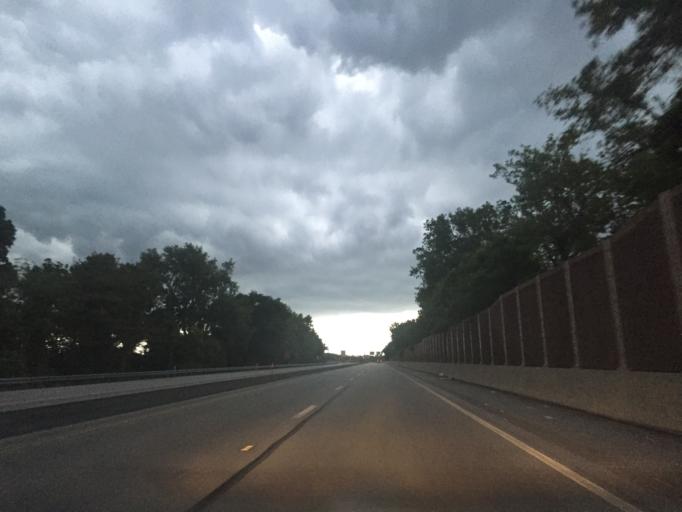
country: US
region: Pennsylvania
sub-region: York County
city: Spry
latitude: 39.9246
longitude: -76.7072
